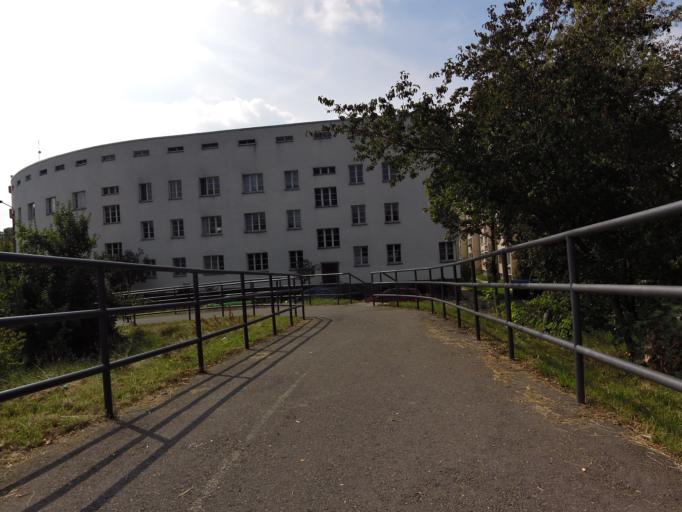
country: DE
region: Saxony
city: Leipzig
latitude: 51.3713
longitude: 12.3489
